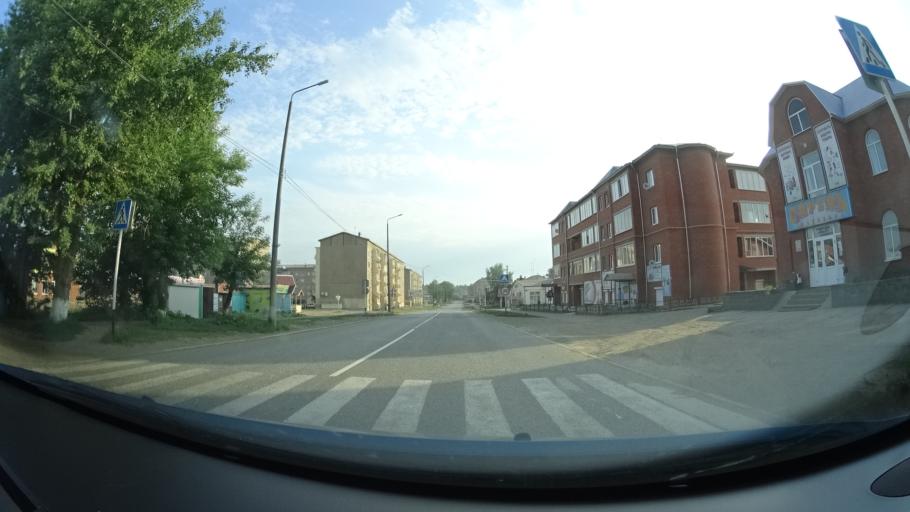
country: RU
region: Perm
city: Barda
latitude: 56.9266
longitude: 55.5914
